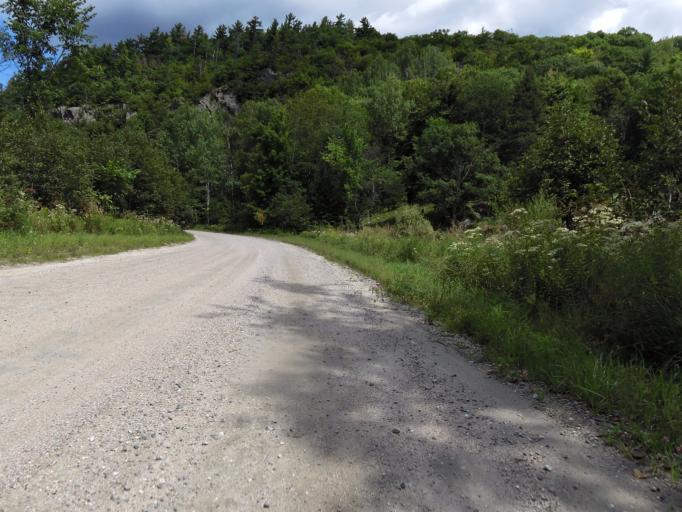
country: CA
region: Quebec
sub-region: Outaouais
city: Wakefield
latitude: 45.8003
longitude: -76.0261
